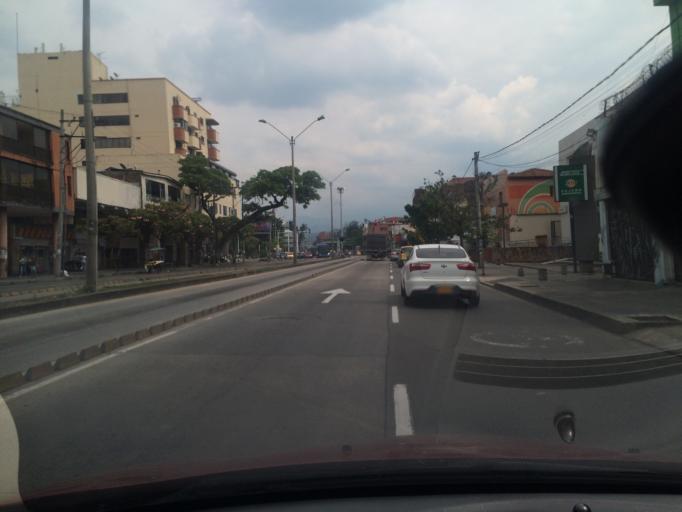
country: CO
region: Valle del Cauca
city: Cali
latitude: 3.4336
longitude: -76.5421
